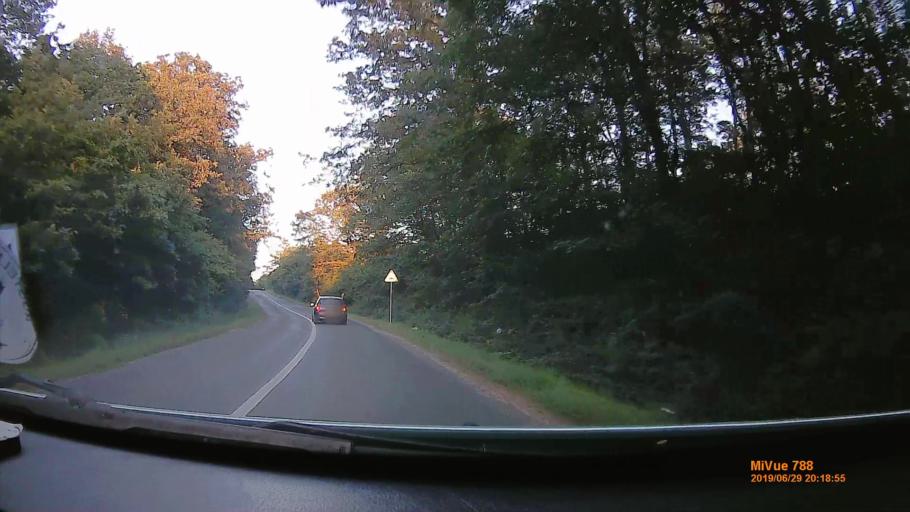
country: HU
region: Pest
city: Paty
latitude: 47.5024
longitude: 18.8608
